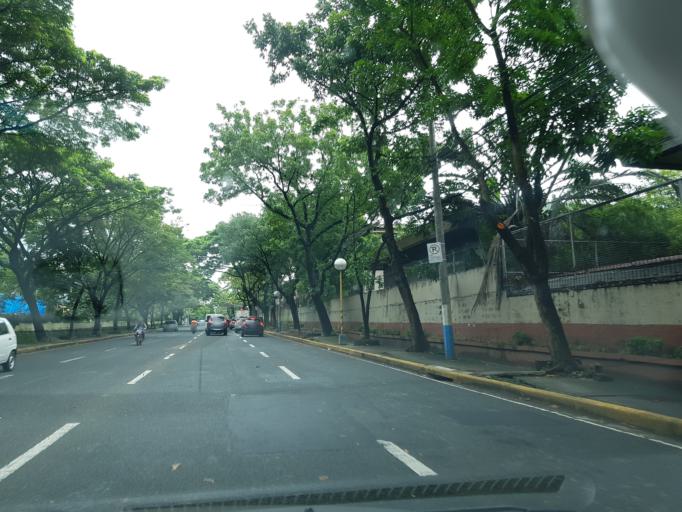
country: PH
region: Metro Manila
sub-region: Pasig
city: Pasig City
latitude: 14.5828
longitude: 121.0707
